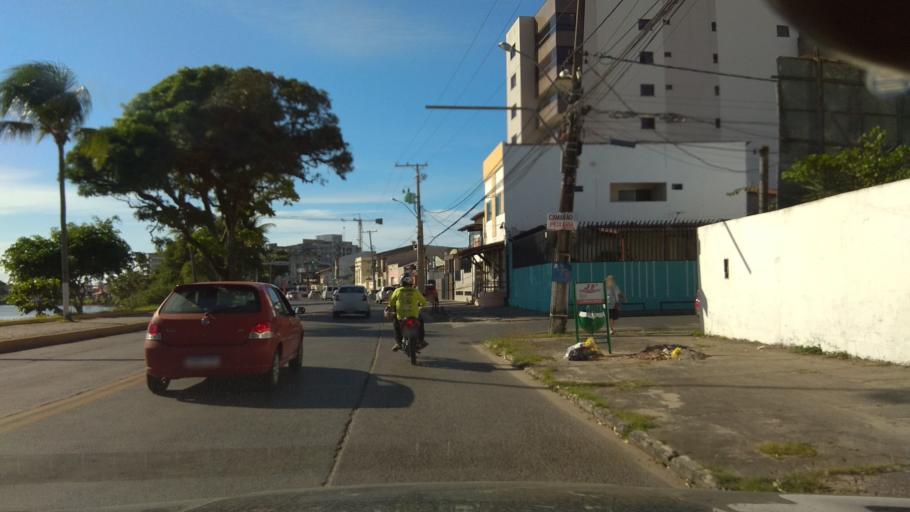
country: BR
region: Bahia
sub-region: Ilheus
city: Ilheus
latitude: -14.8114
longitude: -39.0328
